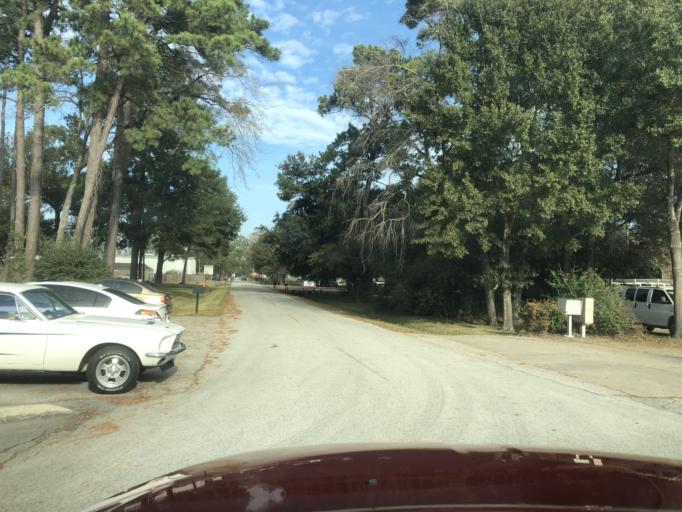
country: US
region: Texas
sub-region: Harris County
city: Hudson
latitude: 29.9958
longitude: -95.4745
